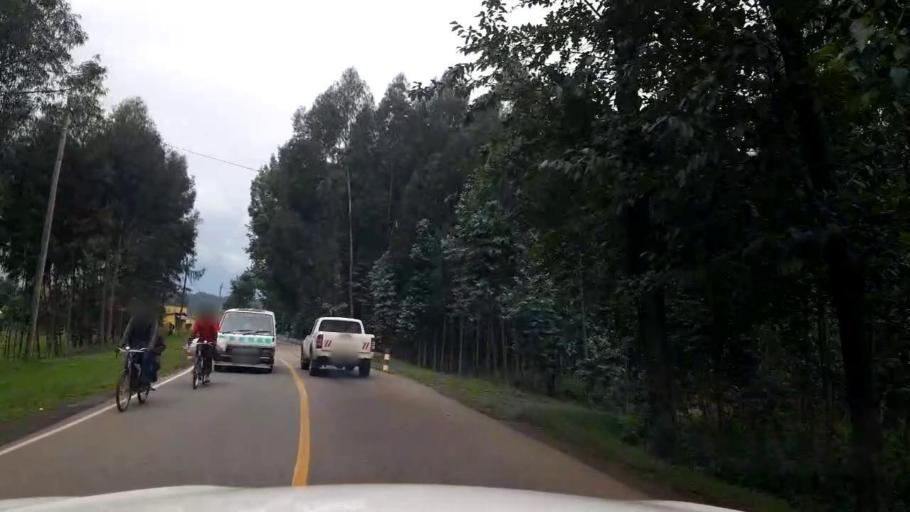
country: RW
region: Northern Province
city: Musanze
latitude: -1.4652
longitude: 29.6166
